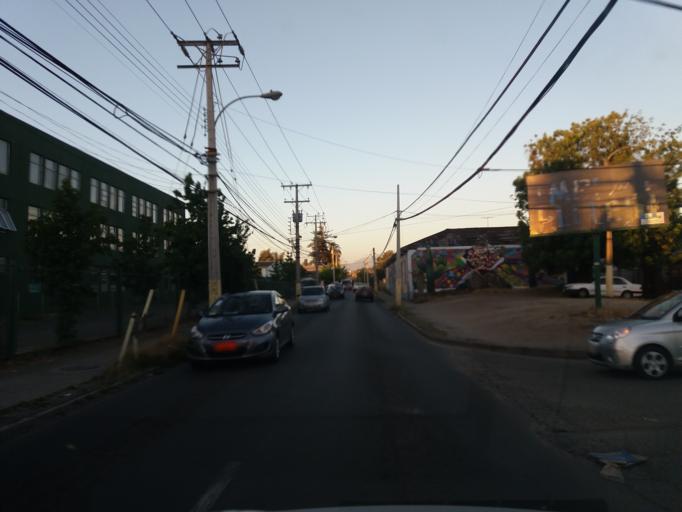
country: CL
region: Valparaiso
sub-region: Provincia de Quillota
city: Quillota
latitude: -32.8904
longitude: -71.2616
